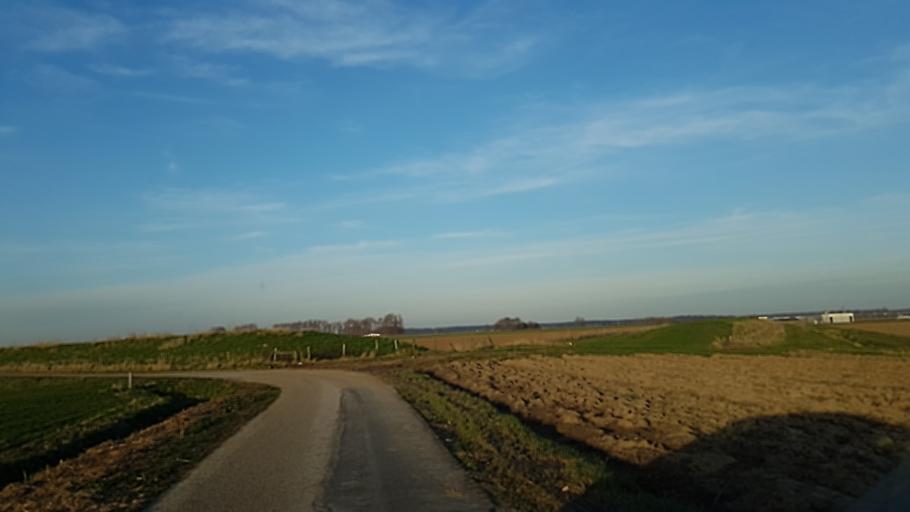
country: NL
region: North Brabant
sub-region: Gemeente Woensdrecht
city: Woensdrecht
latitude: 51.3879
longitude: 4.2683
